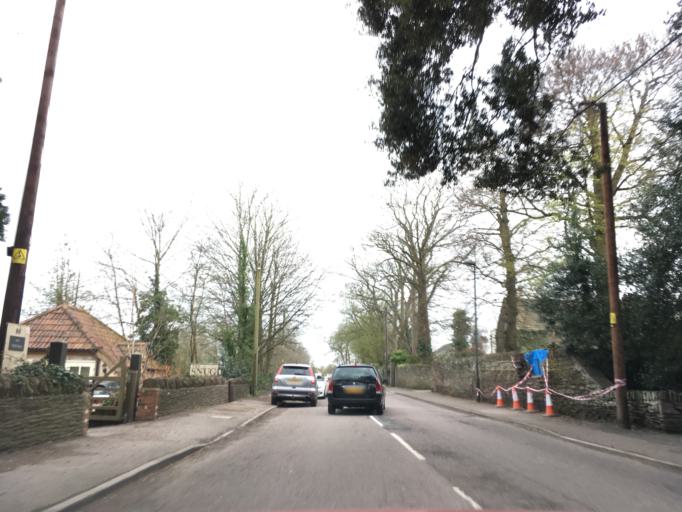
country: GB
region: England
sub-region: South Gloucestershire
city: Winterbourne
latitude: 51.5233
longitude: -2.4994
